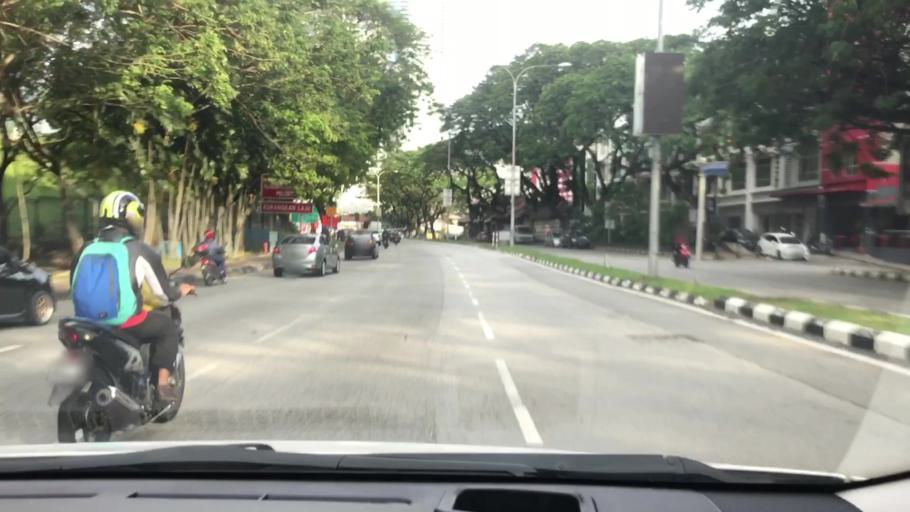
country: MY
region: Kuala Lumpur
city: Kuala Lumpur
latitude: 3.1169
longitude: 101.6685
